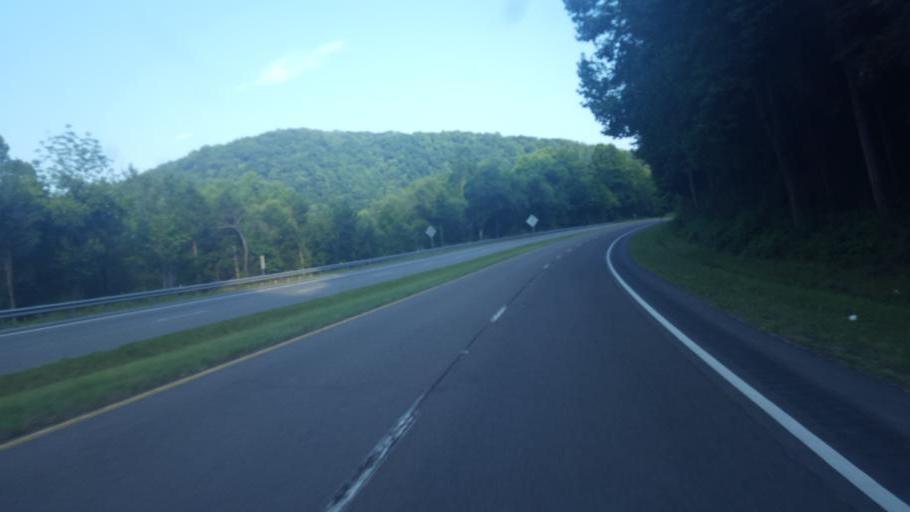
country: US
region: Tennessee
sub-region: Hawkins County
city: Mount Carmel
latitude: 36.6963
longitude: -82.7554
